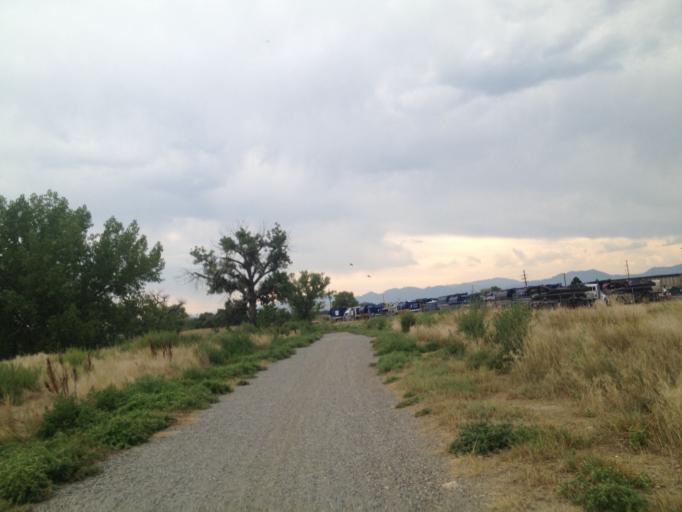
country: US
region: Colorado
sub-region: Boulder County
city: Lafayette
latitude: 40.0081
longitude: -105.0535
